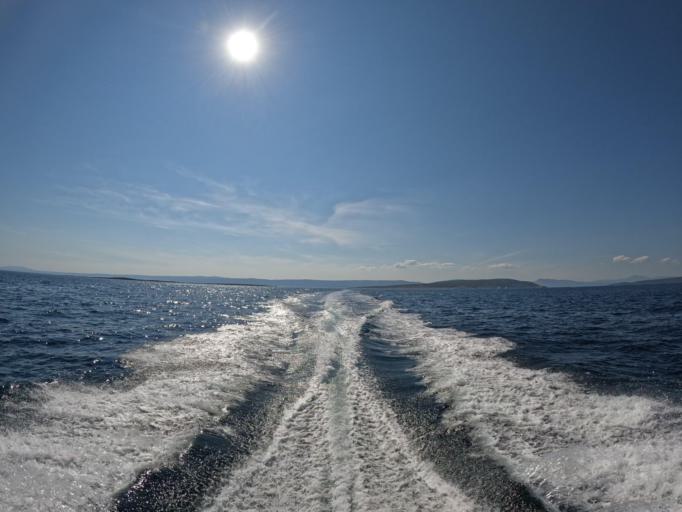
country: HR
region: Primorsko-Goranska
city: Punat
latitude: 44.9542
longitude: 14.5898
